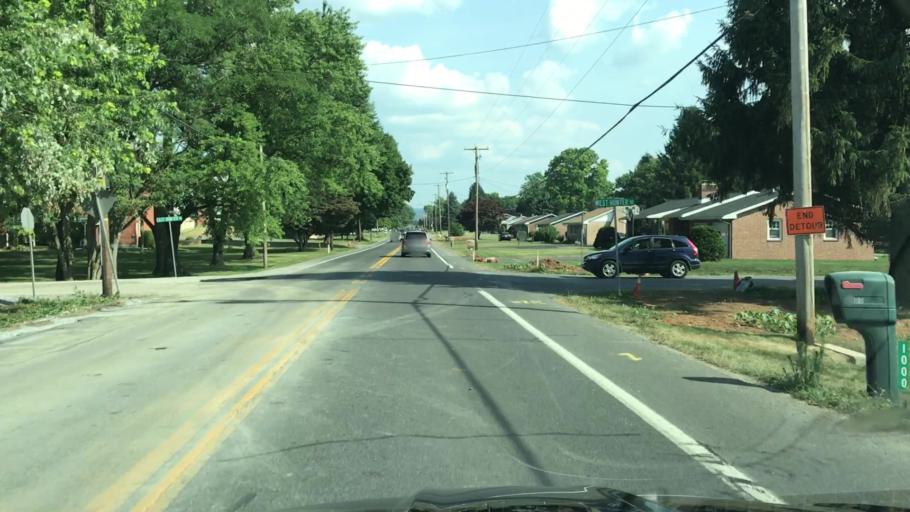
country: US
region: Pennsylvania
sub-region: Cumberland County
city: Carlisle
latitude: 40.1857
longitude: -77.1575
